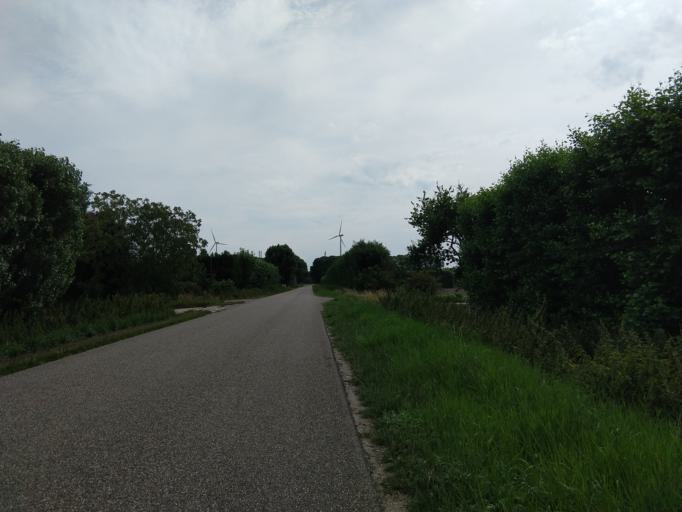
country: NL
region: Zeeland
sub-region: Gemeente Borsele
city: Borssele
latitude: 51.4882
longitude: 3.7109
